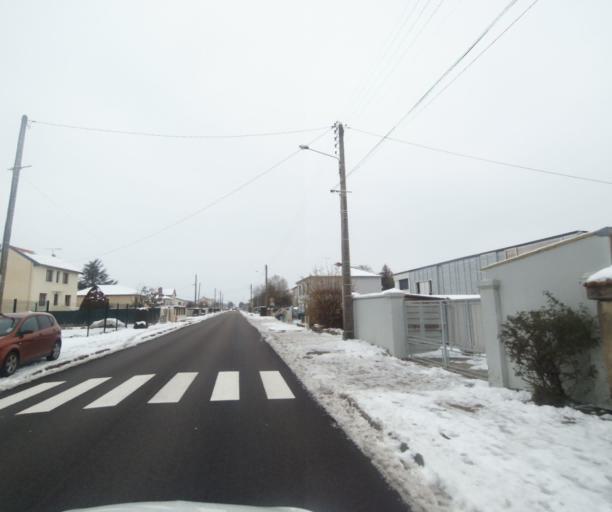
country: FR
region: Champagne-Ardenne
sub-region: Departement de la Haute-Marne
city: Villiers-en-Lieu
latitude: 48.5929
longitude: 4.8690
